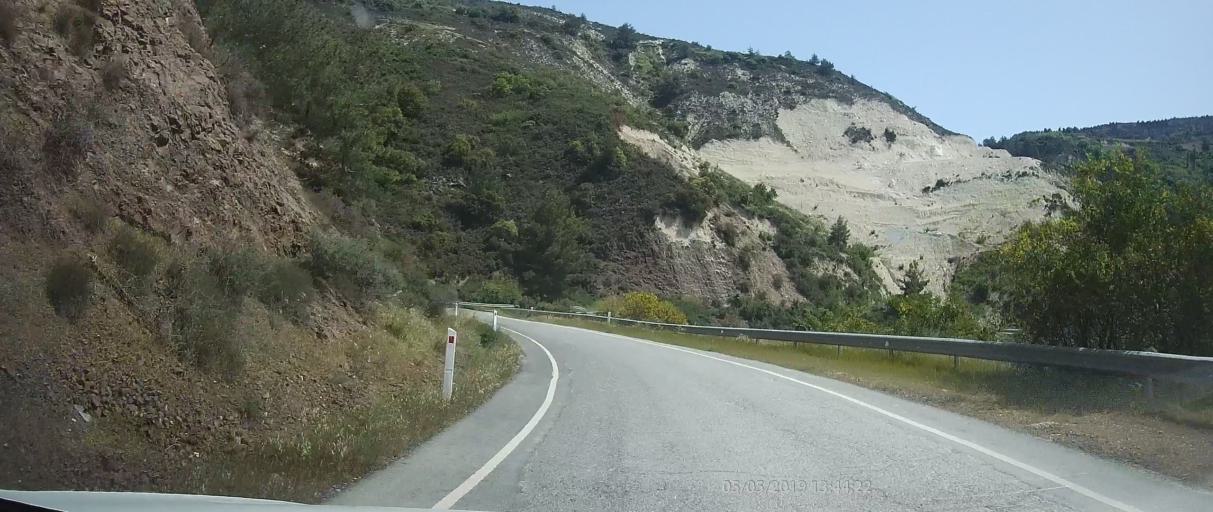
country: CY
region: Limassol
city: Pachna
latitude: 34.8705
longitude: 32.7907
